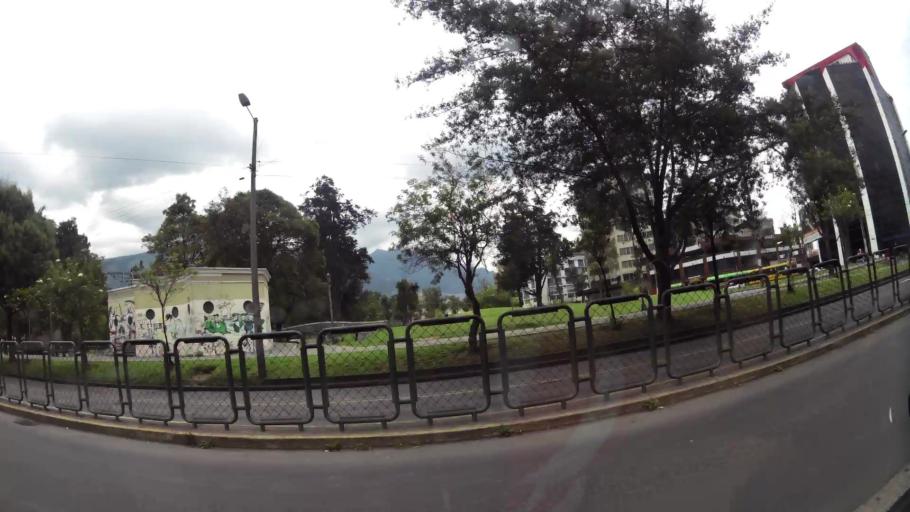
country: EC
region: Pichincha
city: Quito
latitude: -0.2150
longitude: -78.5009
